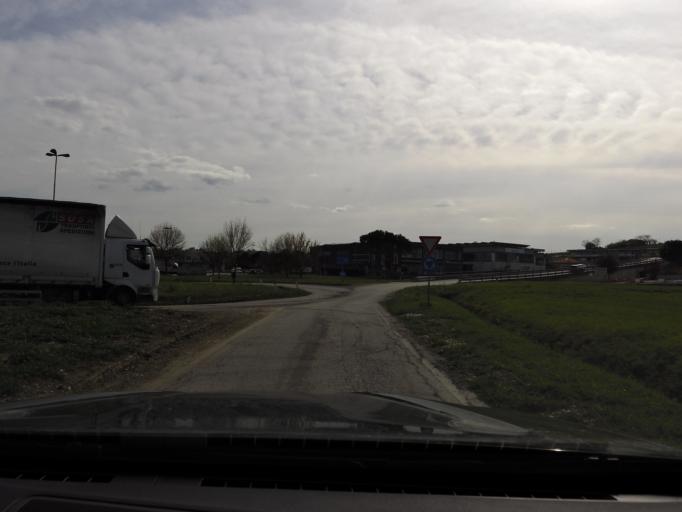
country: IT
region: The Marches
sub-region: Provincia di Ancona
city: Camerano
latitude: 43.5165
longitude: 13.5303
